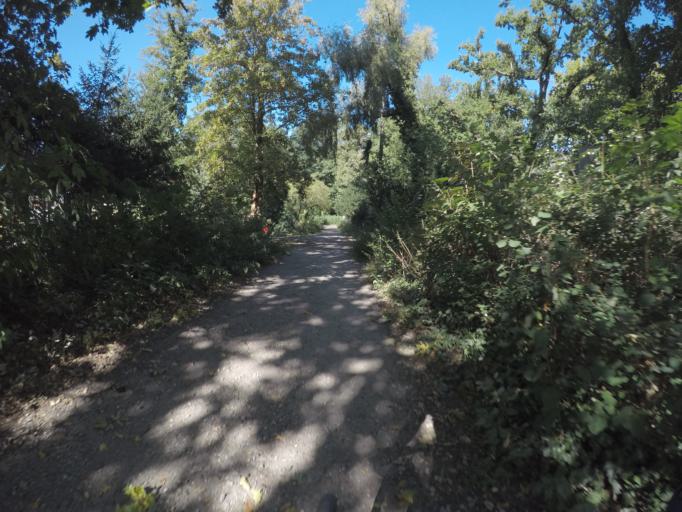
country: DE
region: Berlin
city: Tegel
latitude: 52.5917
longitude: 13.2694
